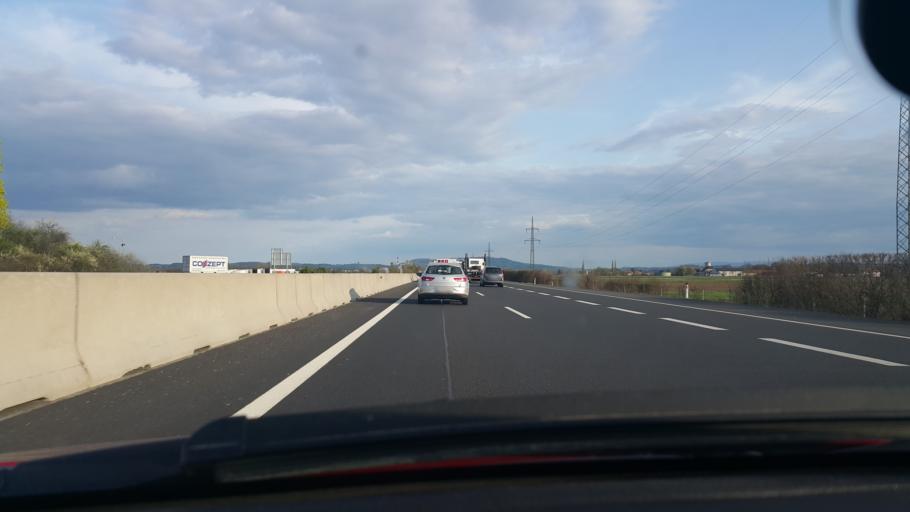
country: AT
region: Styria
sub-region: Politischer Bezirk Graz-Umgebung
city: Zettling
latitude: 46.9619
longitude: 15.4382
